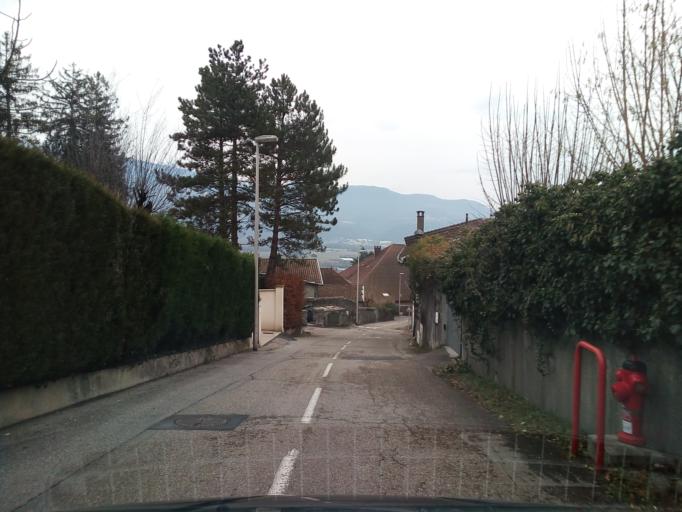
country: FR
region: Rhone-Alpes
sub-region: Departement de l'Isere
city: Meylan
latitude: 45.2239
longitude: 5.7790
